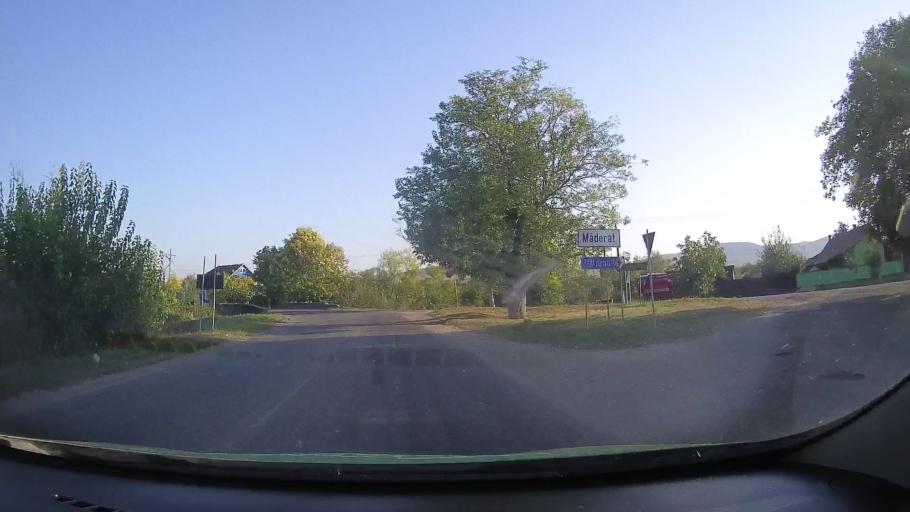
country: RO
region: Arad
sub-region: Comuna Pancota
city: Maderat
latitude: 46.3050
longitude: 21.7090
